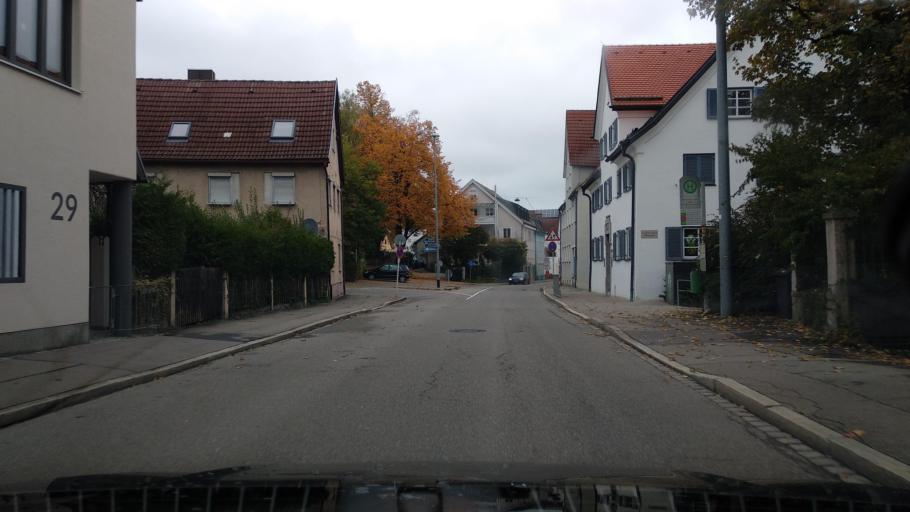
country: DE
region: Bavaria
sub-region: Swabia
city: Kempten (Allgaeu)
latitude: 47.7308
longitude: 10.3111
